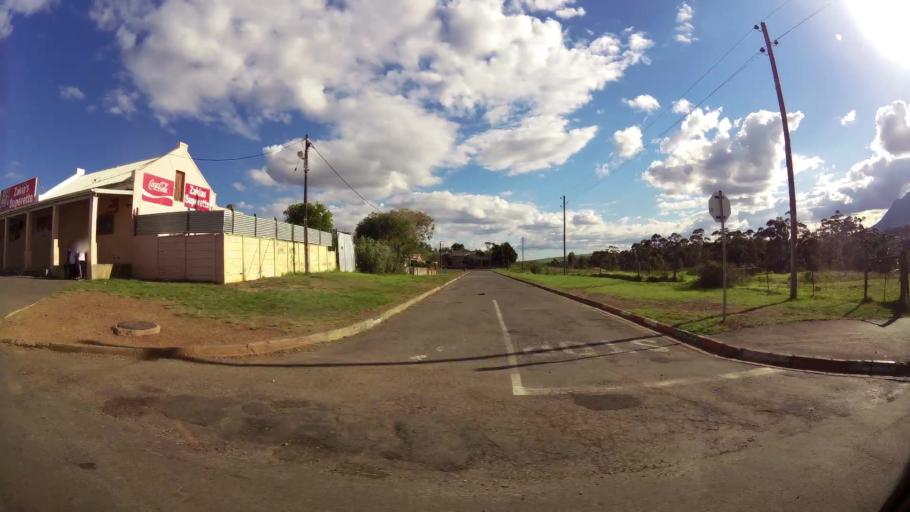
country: ZA
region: Western Cape
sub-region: Overberg District Municipality
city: Swellendam
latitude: -34.0316
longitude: 20.4428
